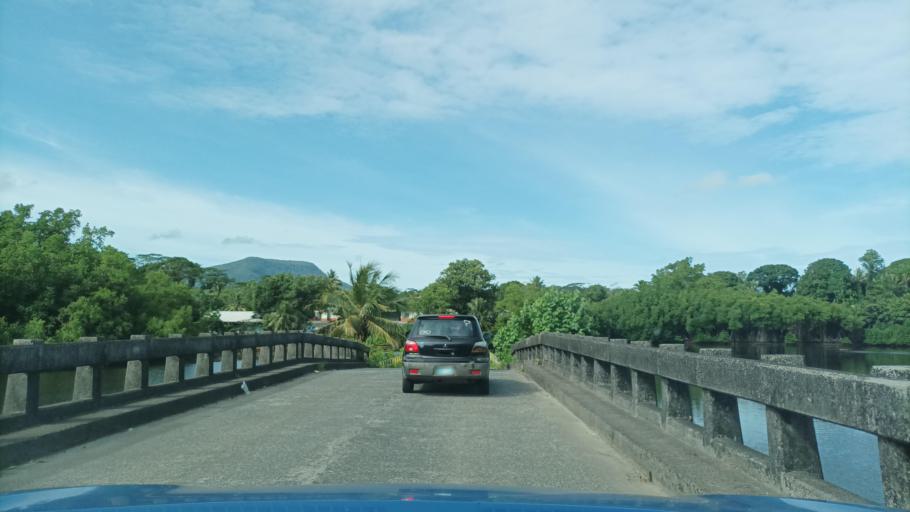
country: FM
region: Pohnpei
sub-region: Kolonia Municipality
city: Kolonia
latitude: 6.9542
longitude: 158.2270
